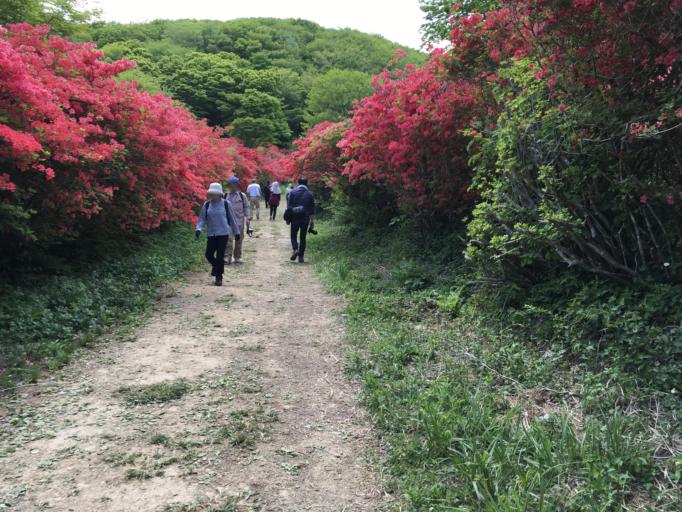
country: JP
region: Iwate
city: Ofunato
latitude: 38.8501
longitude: 141.4711
